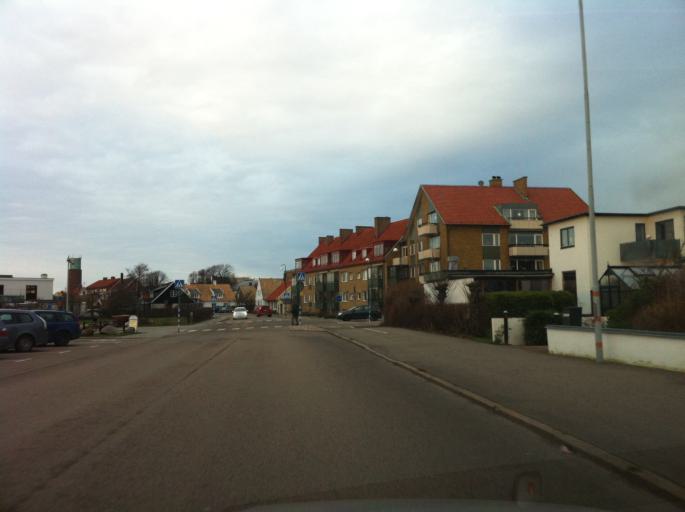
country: SE
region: Skane
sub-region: Hoganas Kommun
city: Hoganas
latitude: 56.1989
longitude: 12.5544
